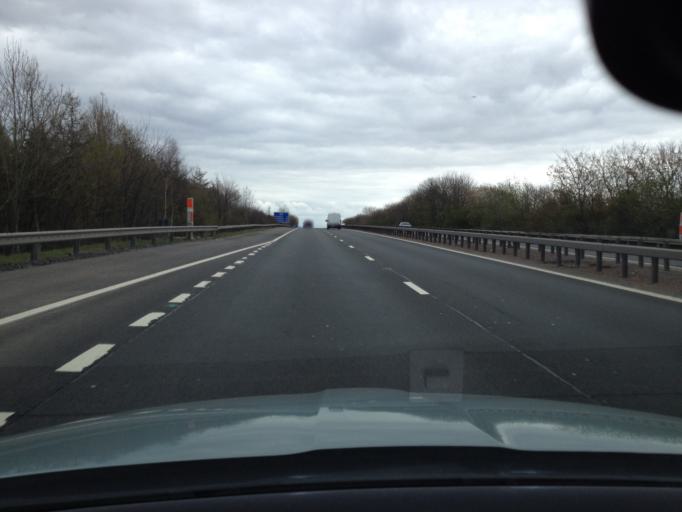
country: GB
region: Scotland
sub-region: West Lothian
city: Whitburn
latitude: 55.8706
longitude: -3.6899
